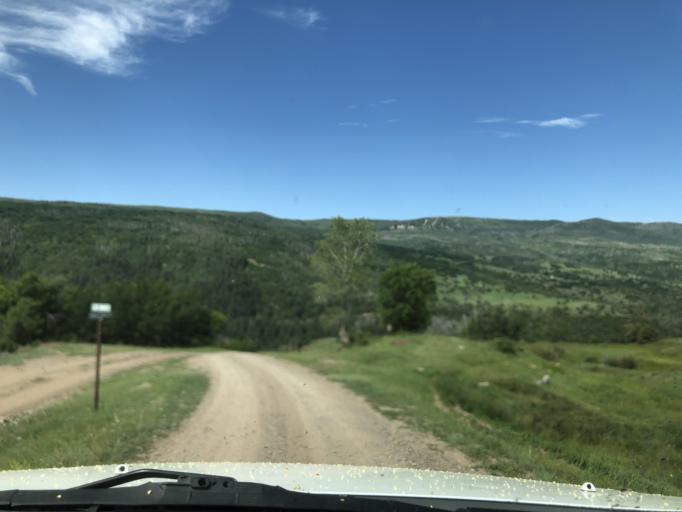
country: US
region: Colorado
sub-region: Delta County
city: Paonia
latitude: 38.9982
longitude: -107.3472
